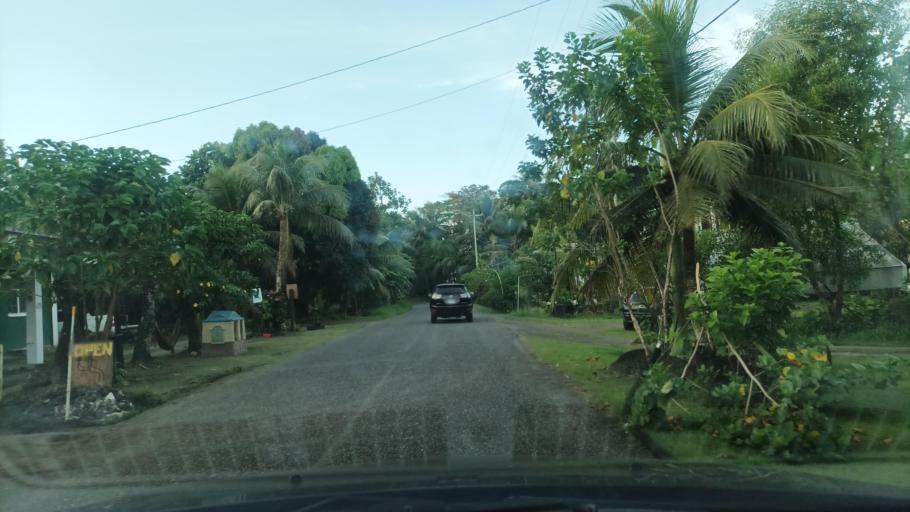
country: FM
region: Kosrae
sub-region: Lelu Municipality
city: Lelu
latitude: 5.3160
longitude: 163.0338
